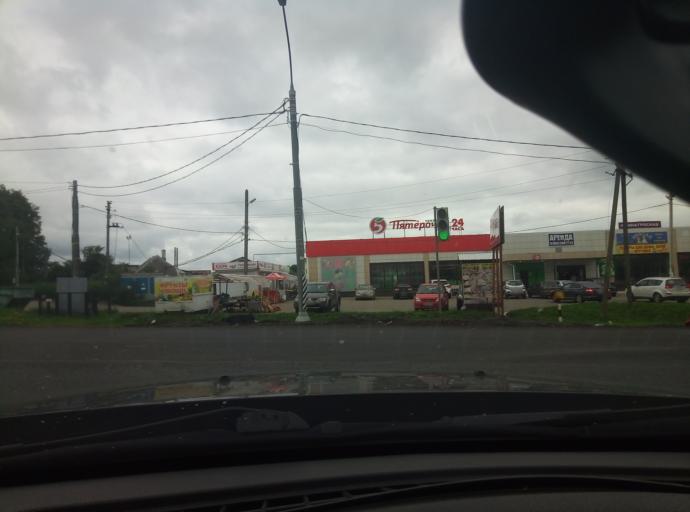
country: RU
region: Kaluga
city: Belousovo
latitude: 55.0923
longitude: 36.6651
